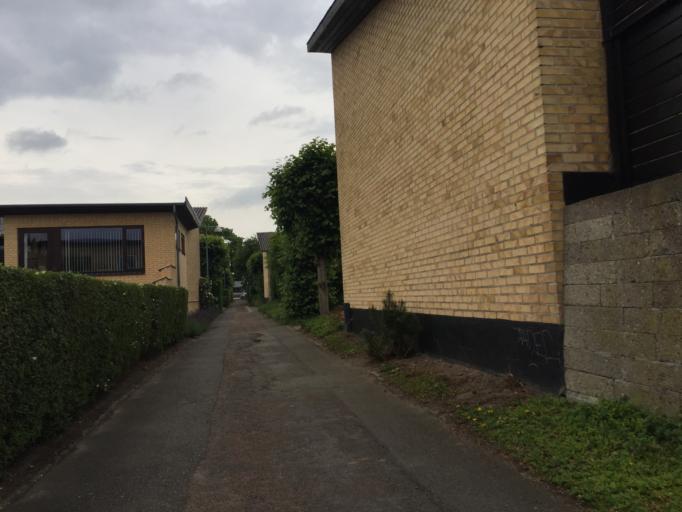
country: DK
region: South Denmark
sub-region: Odense Kommune
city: Odense
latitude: 55.3776
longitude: 10.4015
